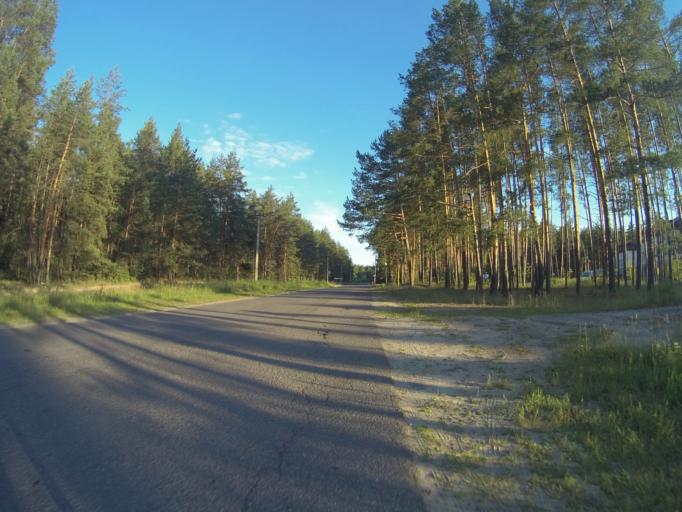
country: RU
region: Vladimir
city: Kommunar
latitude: 56.1355
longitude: 40.4903
